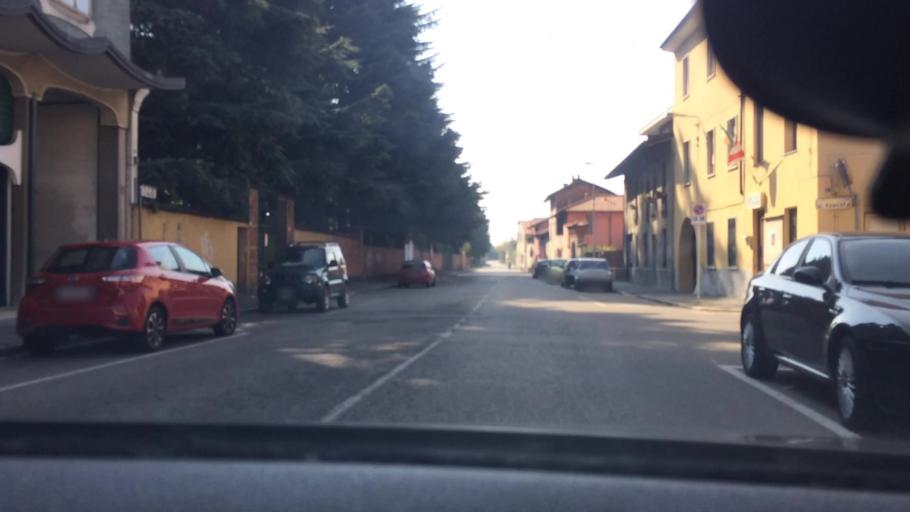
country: IT
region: Lombardy
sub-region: Citta metropolitana di Milano
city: Busto Garolfo
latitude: 45.5445
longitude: 8.8832
